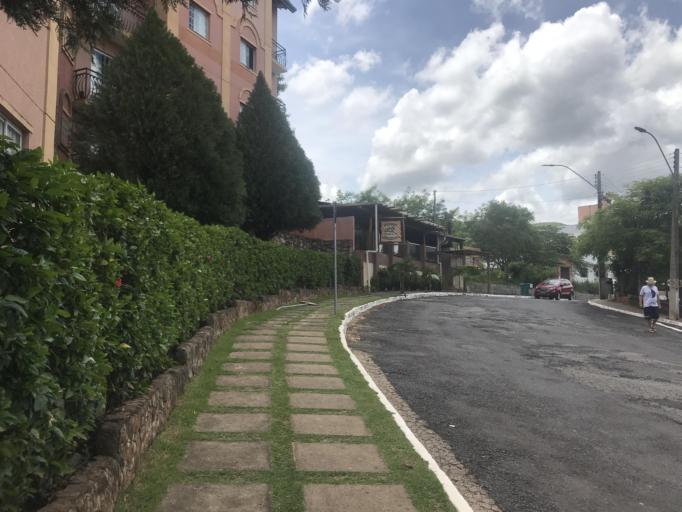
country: BR
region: Goias
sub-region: Caldas Novas
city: Caldas Novas
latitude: -17.7687
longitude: -48.7556
